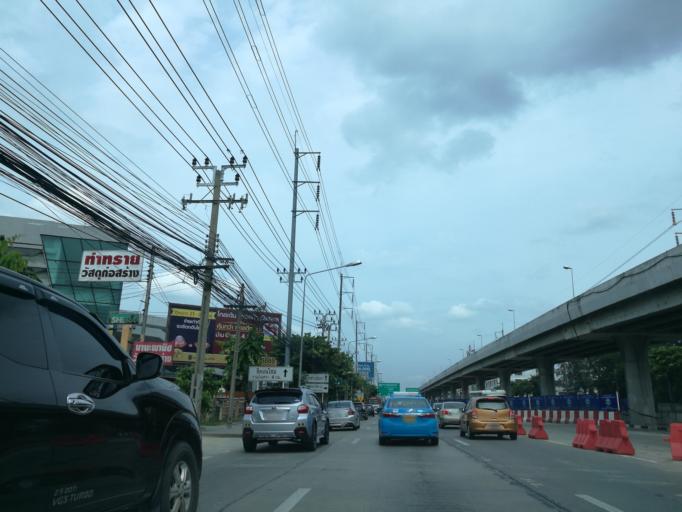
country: TH
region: Bangkok
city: Bang Khen
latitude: 13.8664
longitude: 100.6114
